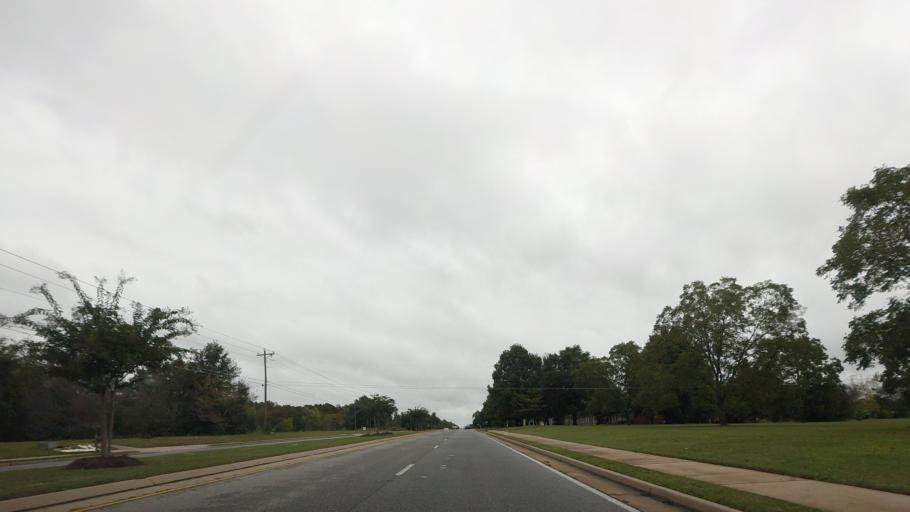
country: US
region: Georgia
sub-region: Houston County
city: Perry
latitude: 32.5107
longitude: -83.6624
